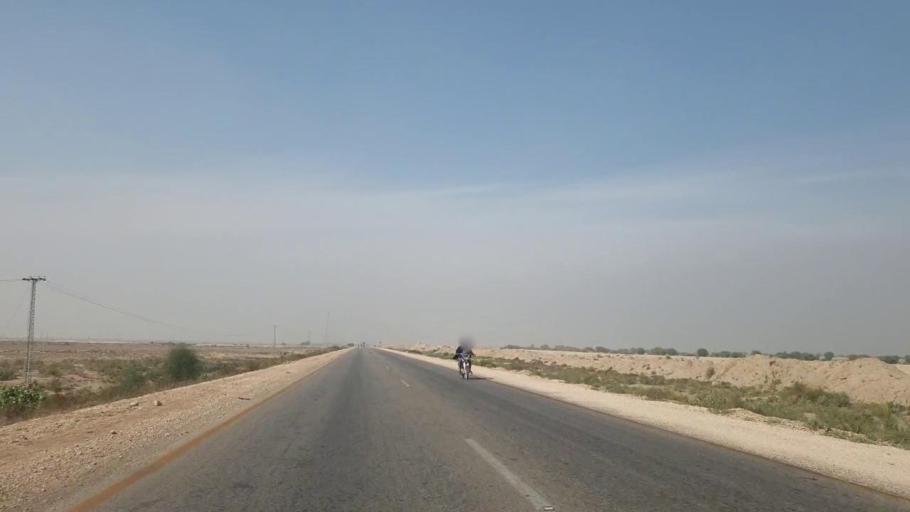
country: PK
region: Sindh
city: Sann
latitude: 25.9135
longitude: 68.2229
